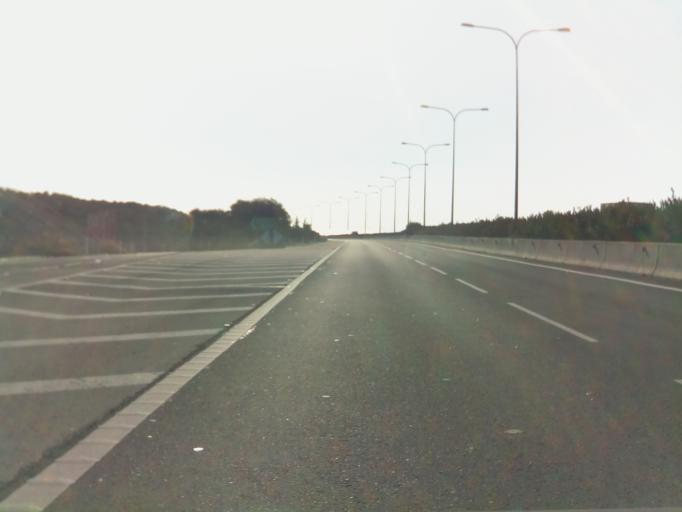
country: CY
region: Limassol
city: Pissouri
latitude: 34.6727
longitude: 32.6111
